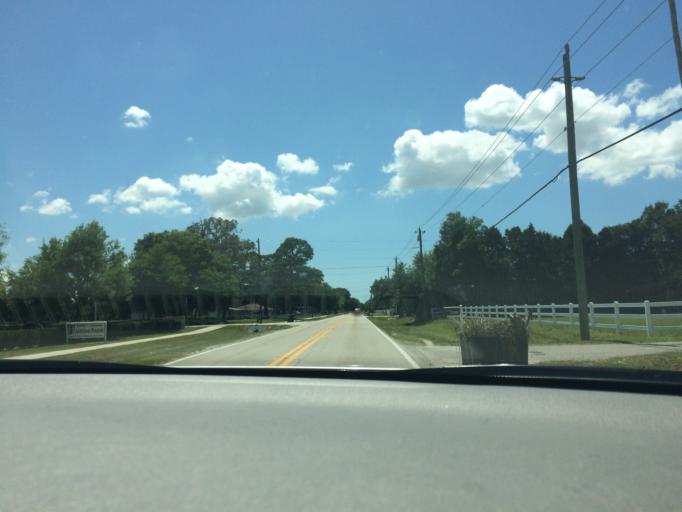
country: US
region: Florida
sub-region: Manatee County
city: Samoset
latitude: 27.4800
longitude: -82.4895
